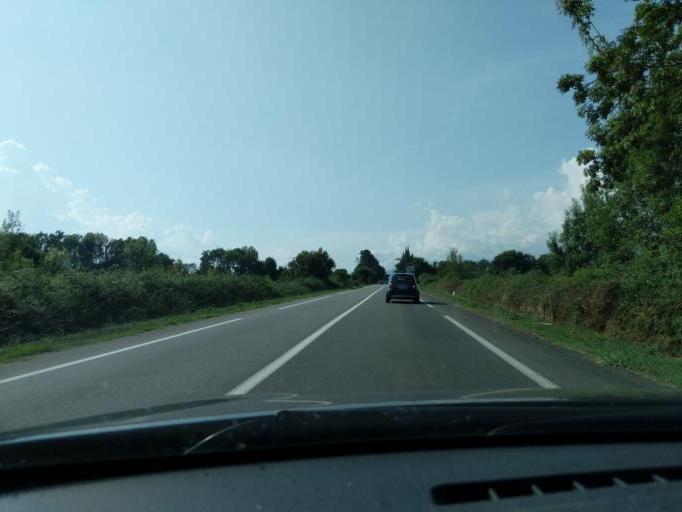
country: FR
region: Corsica
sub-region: Departement de la Haute-Corse
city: Ghisonaccia
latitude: 41.9626
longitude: 9.3972
